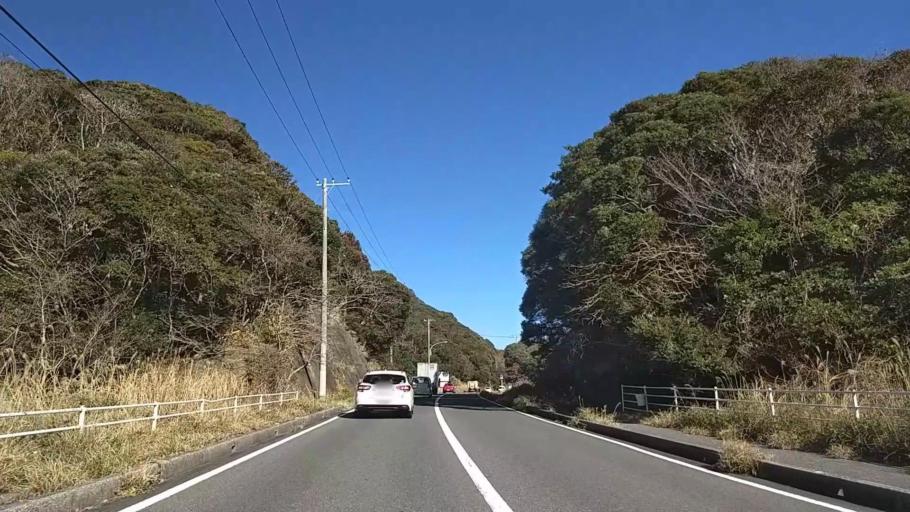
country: JP
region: Chiba
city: Katsuura
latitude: 35.1235
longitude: 140.2304
